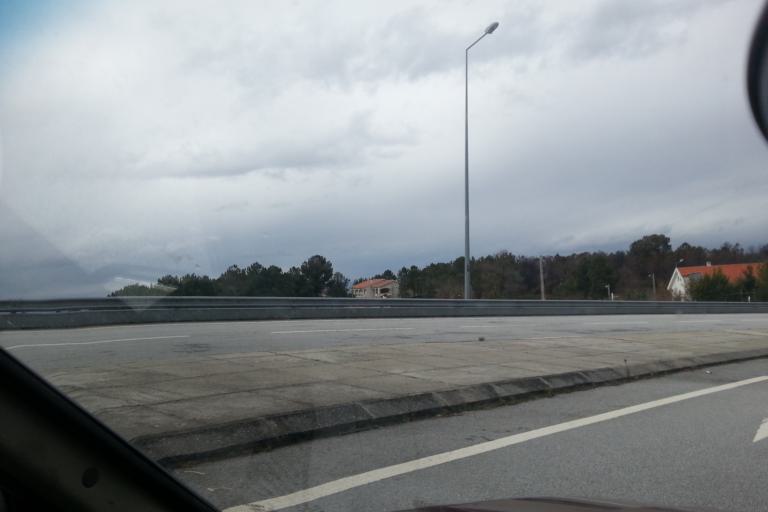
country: PT
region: Guarda
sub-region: Manteigas
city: Manteigas
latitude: 40.4747
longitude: -7.6002
